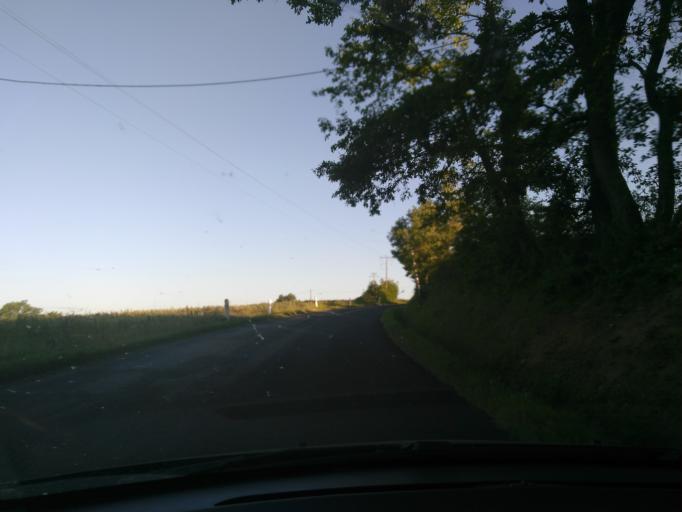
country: FR
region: Midi-Pyrenees
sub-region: Departement du Gers
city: Valence-sur-Baise
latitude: 43.8924
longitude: 0.3610
